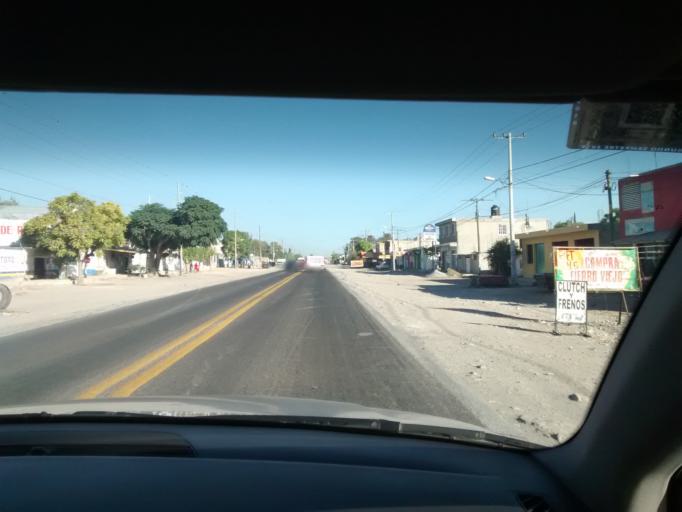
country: MX
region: Puebla
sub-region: Santiago Miahuatlan
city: San Jose Monte Chiquito
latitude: 18.4905
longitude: -97.4614
